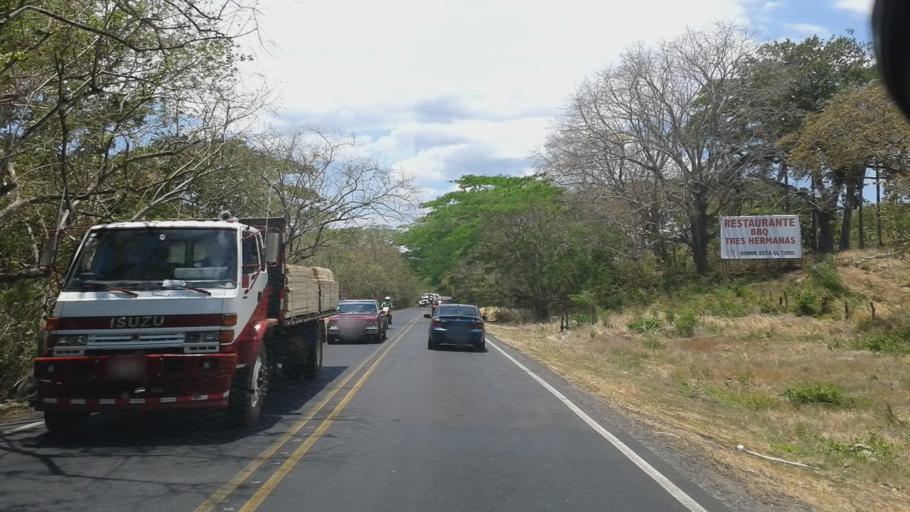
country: CR
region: Puntarenas
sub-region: Canton Central de Puntarenas
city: Puntarenas
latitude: 10.0881
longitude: -84.8465
